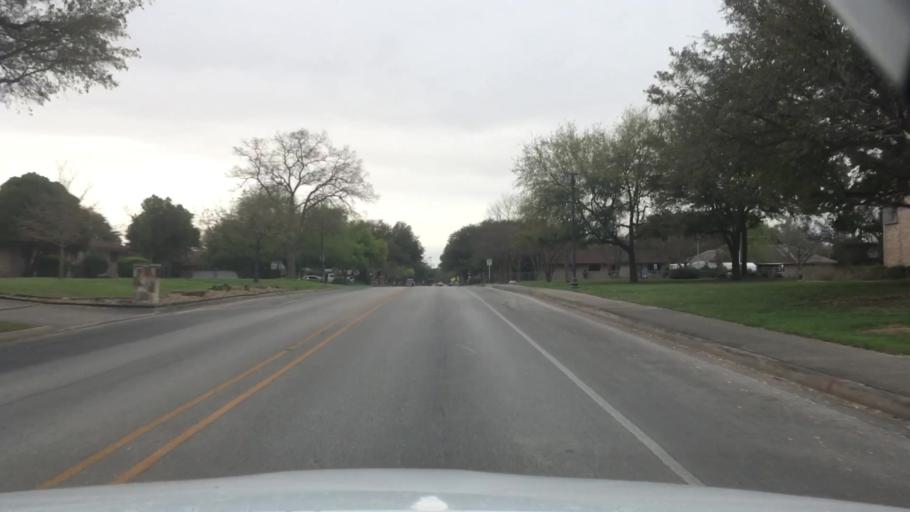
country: US
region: Texas
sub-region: Bexar County
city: Windcrest
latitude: 29.5224
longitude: -98.3816
